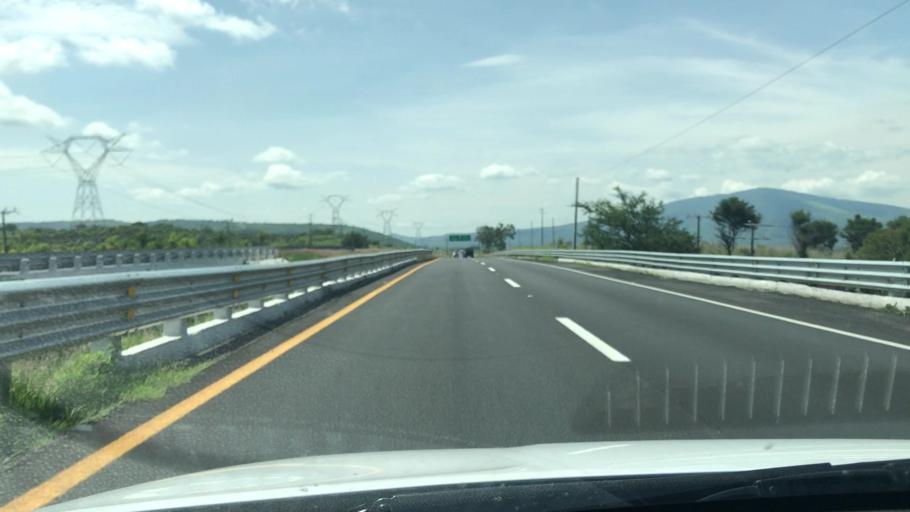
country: MX
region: Jalisco
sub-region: Zapotlanejo
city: La Mezquitera
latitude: 20.5938
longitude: -103.1090
